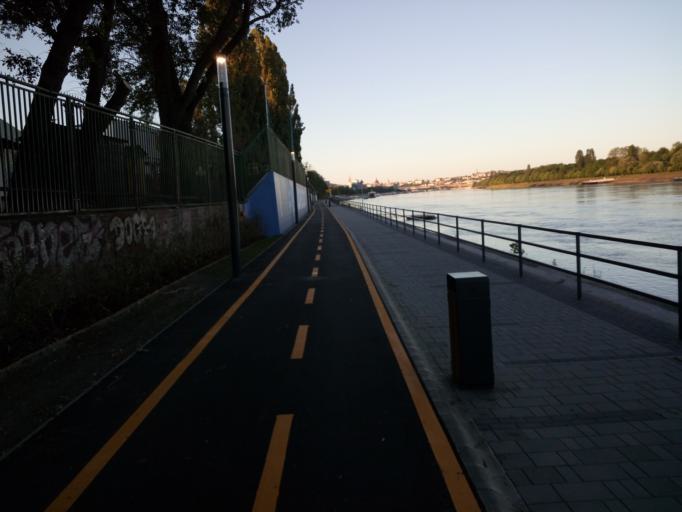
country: HU
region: Budapest
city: Budapest III. keruelet
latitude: 47.5343
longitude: 19.0574
